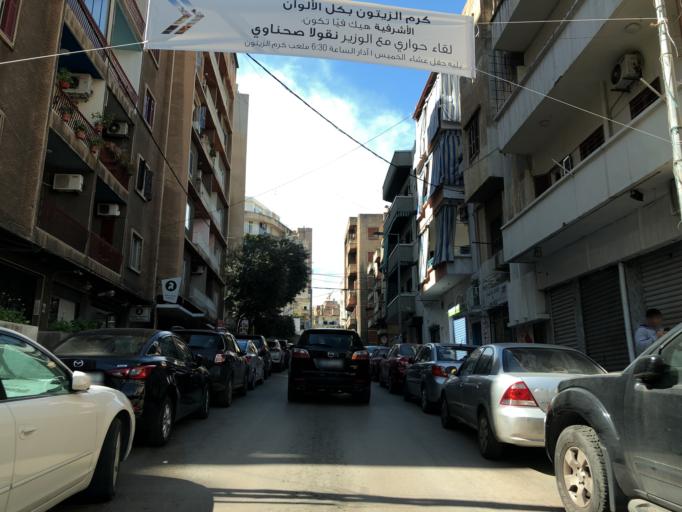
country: LB
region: Beyrouth
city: Beirut
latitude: 33.8872
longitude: 35.5301
